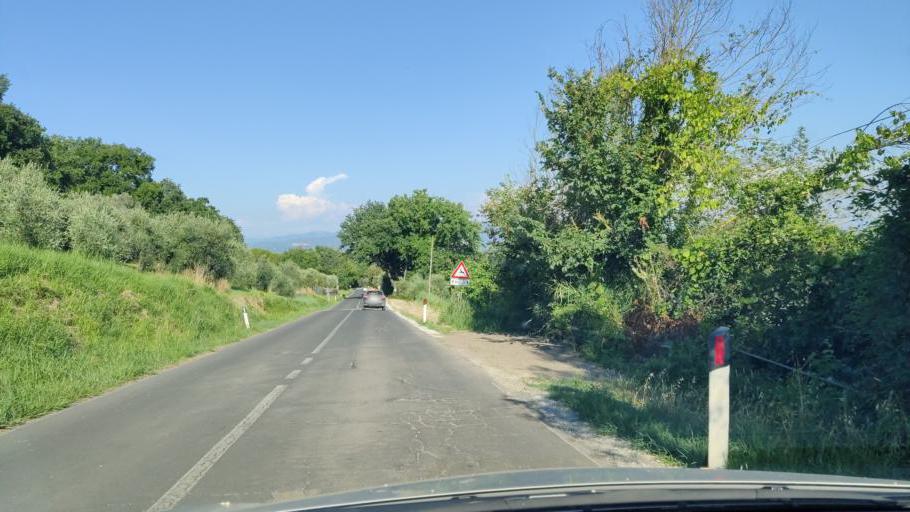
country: IT
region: Umbria
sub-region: Provincia di Terni
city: Penna in Teverina
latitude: 42.4883
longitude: 12.3543
